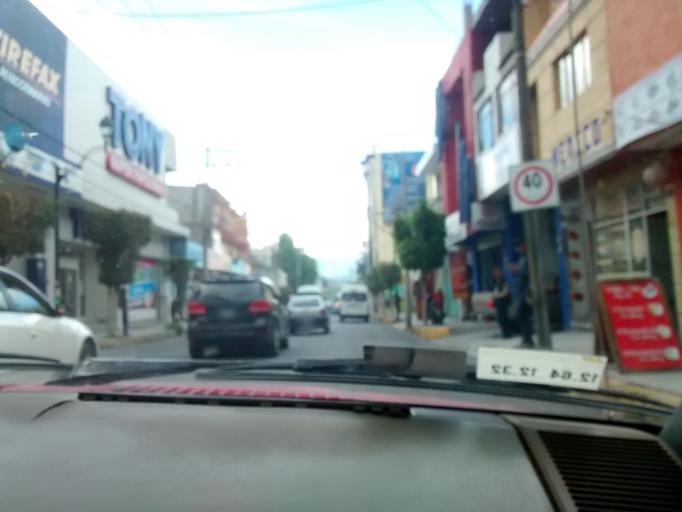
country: MX
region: Puebla
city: Tehuacan
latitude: 18.4628
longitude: -97.3868
